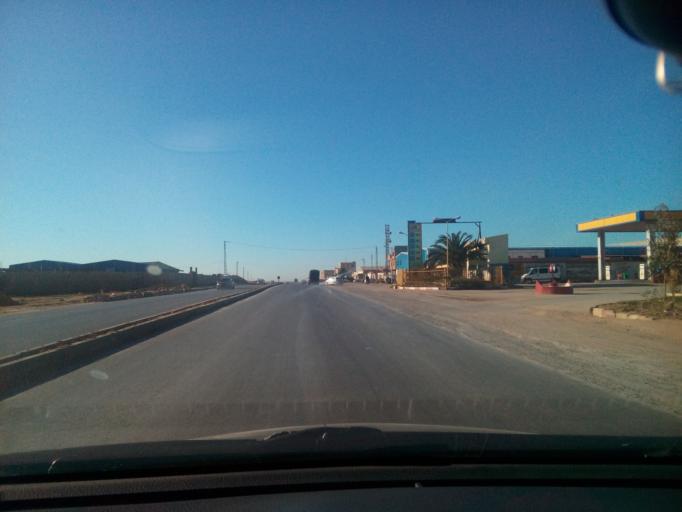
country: DZ
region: Mostaganem
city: Mostaganem
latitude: 35.9113
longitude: 0.1509
